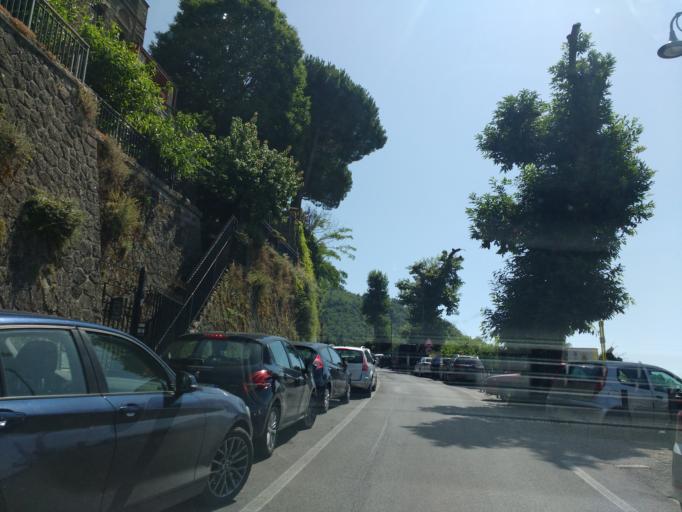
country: IT
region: Latium
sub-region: Citta metropolitana di Roma Capitale
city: Rocca di Papa
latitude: 41.7588
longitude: 12.7077
